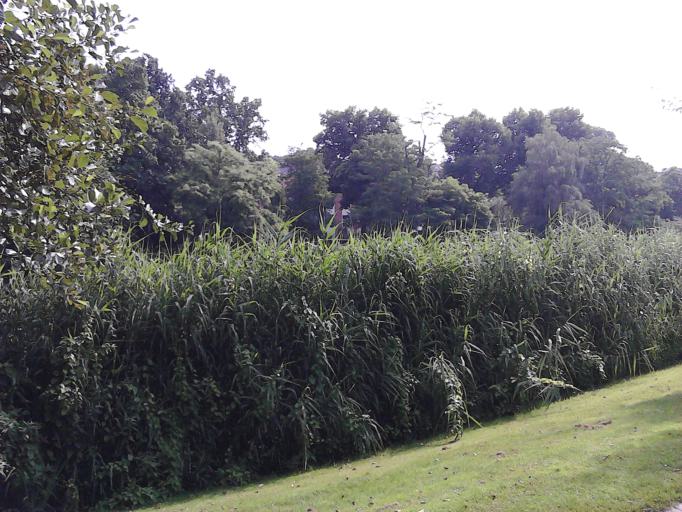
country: DE
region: Bremen
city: Bremen
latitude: 53.0748
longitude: 8.8136
